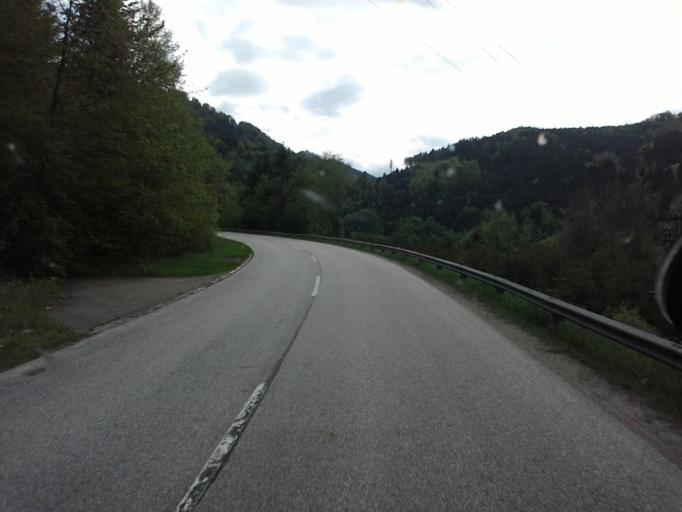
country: AT
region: Styria
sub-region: Politischer Bezirk Liezen
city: Altenmarkt bei Sankt Gallen
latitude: 47.6998
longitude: 14.6845
